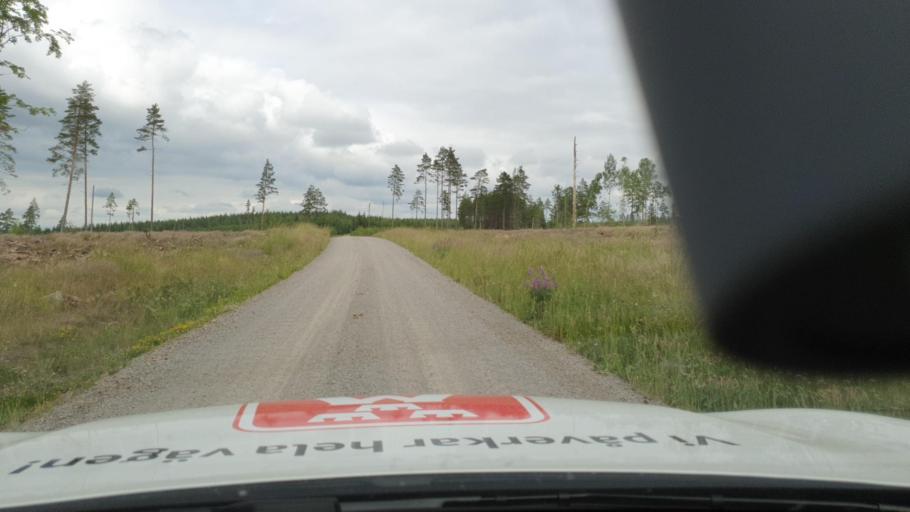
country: SE
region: Vaestra Goetaland
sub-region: Tidaholms Kommun
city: Tidaholm
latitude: 58.1510
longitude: 14.0286
